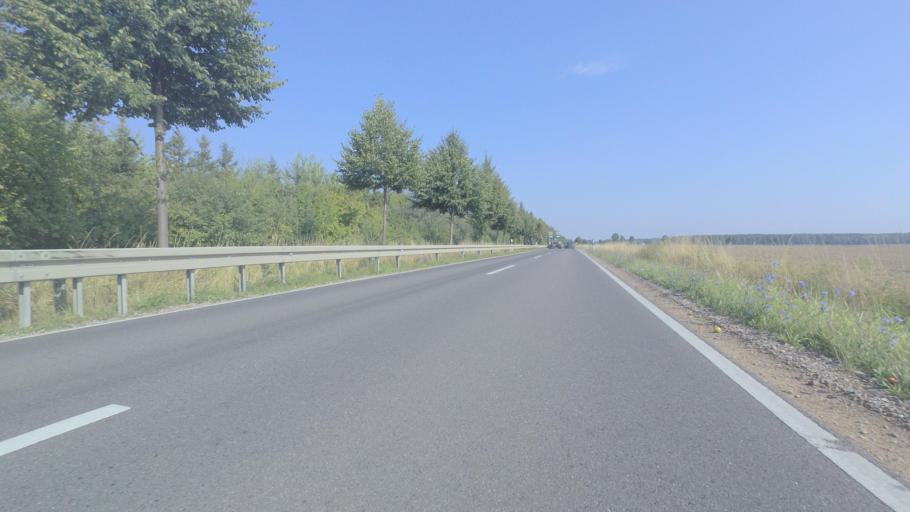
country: DE
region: Mecklenburg-Vorpommern
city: Malchow
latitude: 53.5137
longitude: 12.4230
